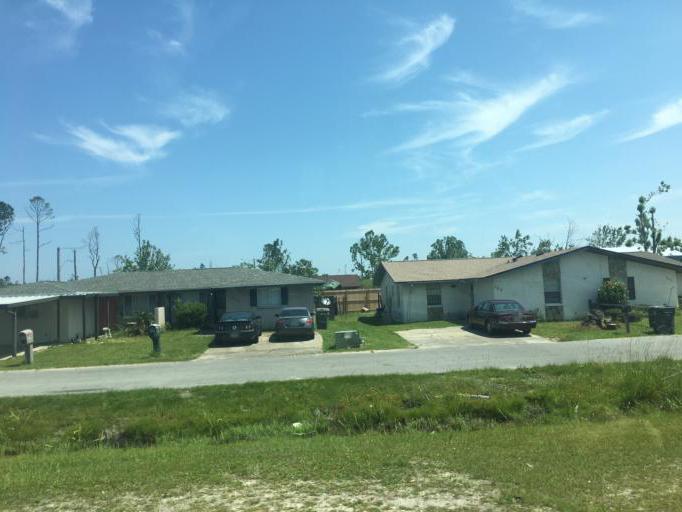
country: US
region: Florida
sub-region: Bay County
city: Lynn Haven
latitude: 30.2187
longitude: -85.6556
